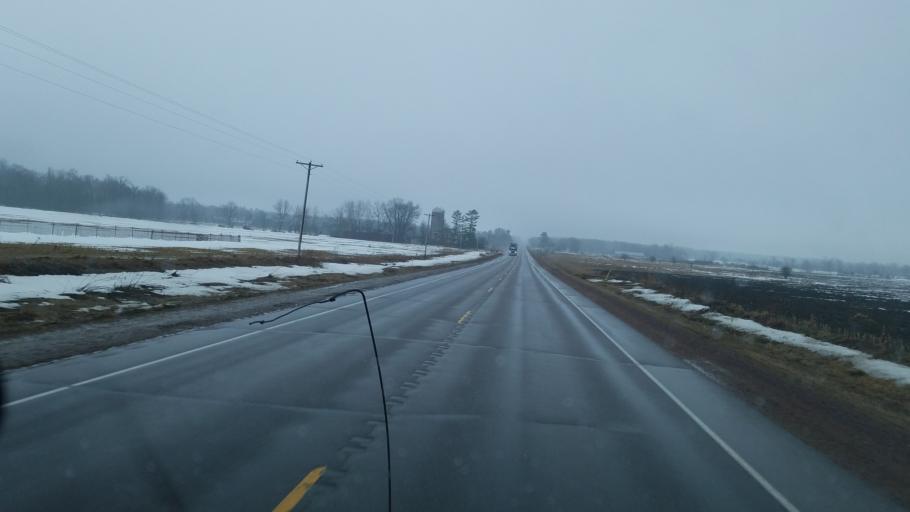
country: US
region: Wisconsin
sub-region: Wood County
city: Marshfield
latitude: 44.5986
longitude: -90.2356
